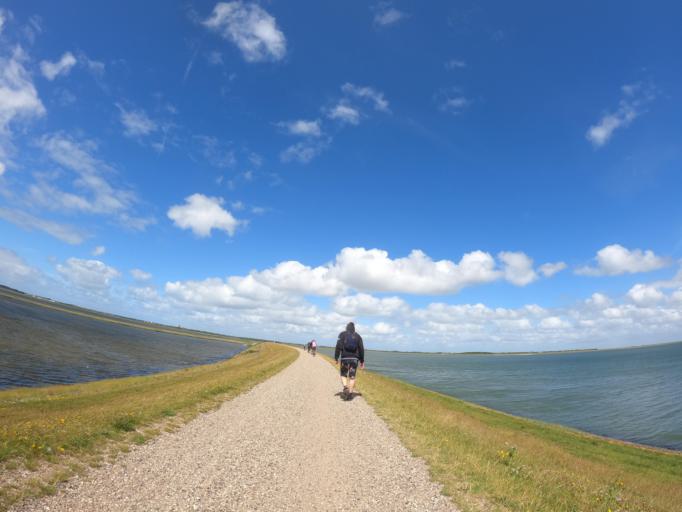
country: DE
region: Schleswig-Holstein
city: Tinnum
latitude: 54.8660
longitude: 8.3337
